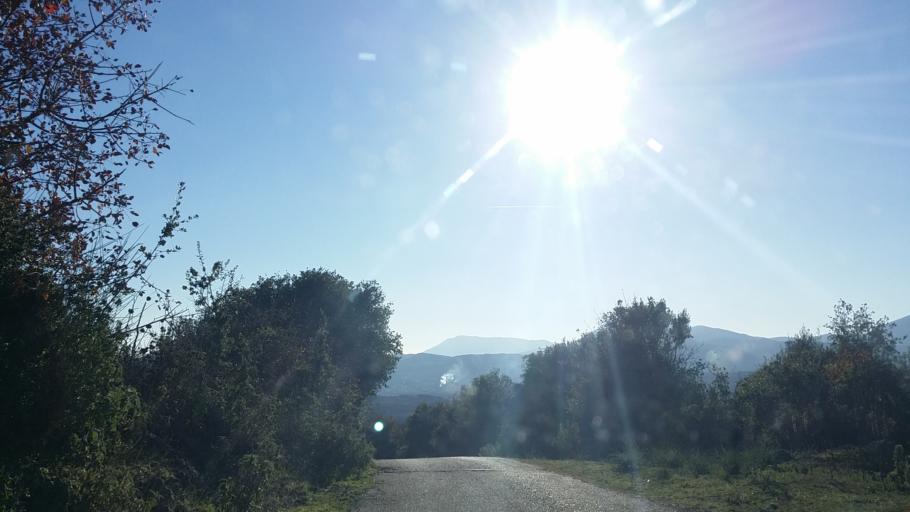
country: GR
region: West Greece
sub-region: Nomos Aitolias kai Akarnanias
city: Fitiai
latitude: 38.7071
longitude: 21.1777
